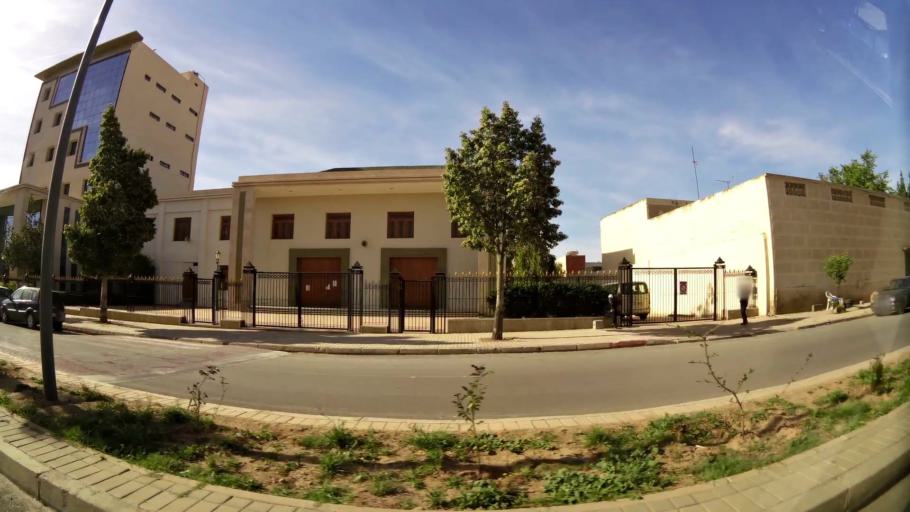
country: MA
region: Oriental
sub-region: Oujda-Angad
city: Oujda
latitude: 34.6681
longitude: -1.8991
